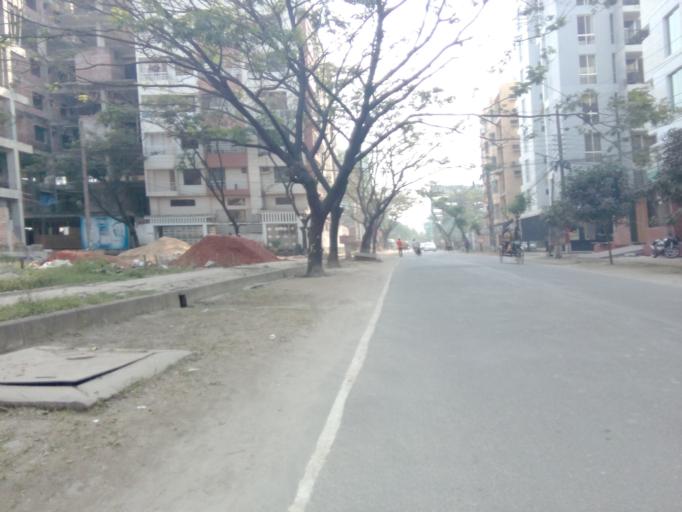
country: BD
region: Dhaka
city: Paltan
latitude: 23.8152
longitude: 90.4342
